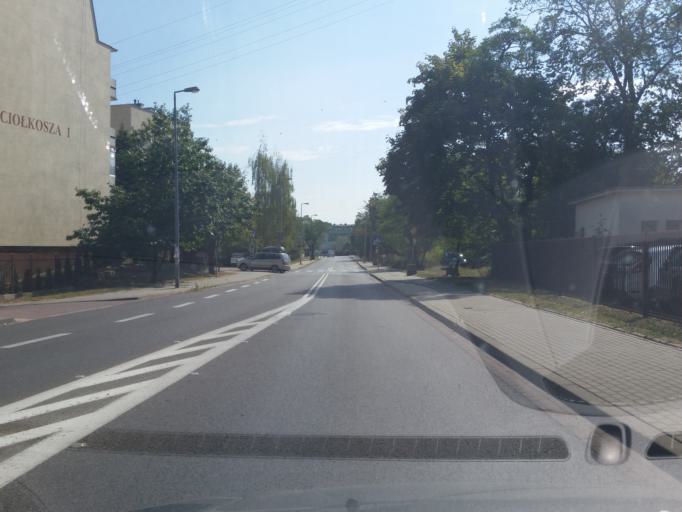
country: PL
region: Masovian Voivodeship
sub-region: Warszawa
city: Bielany
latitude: 52.3274
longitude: 20.9367
